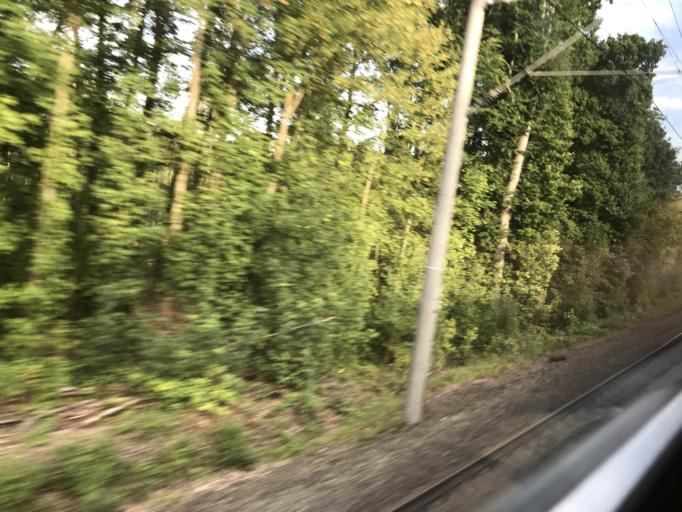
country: DE
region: Hesse
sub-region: Regierungsbezirk Darmstadt
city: Idstein
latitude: 50.1987
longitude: 8.2618
